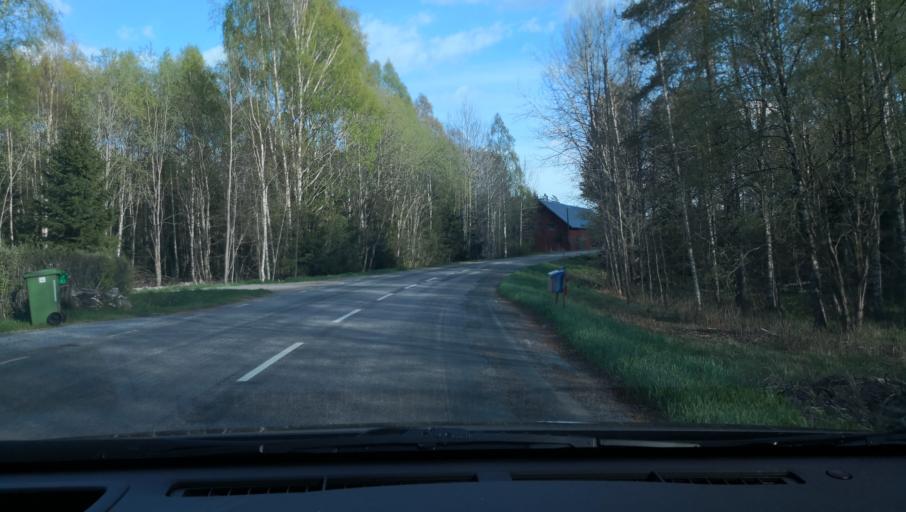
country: SE
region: OErebro
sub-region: Askersunds Kommun
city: Asbro
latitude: 58.9080
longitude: 15.0931
